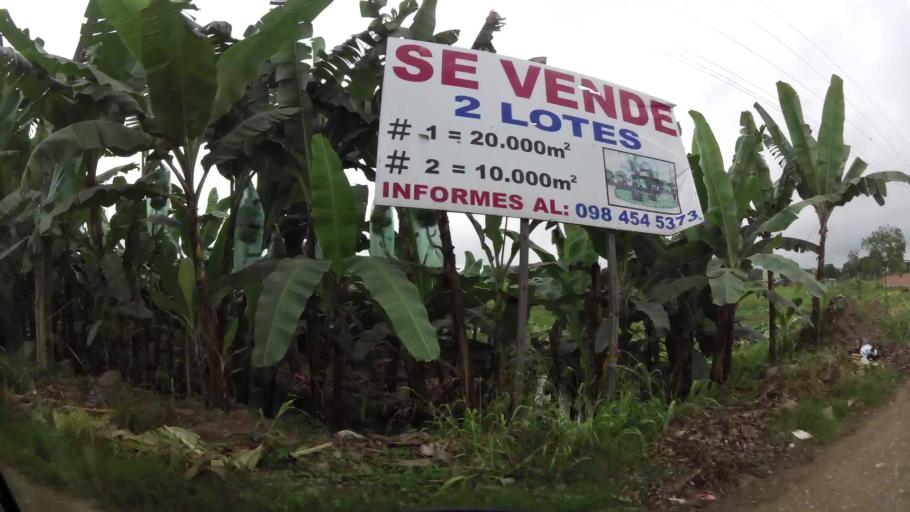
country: EC
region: El Oro
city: Pasaje
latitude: -3.3201
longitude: -79.8105
